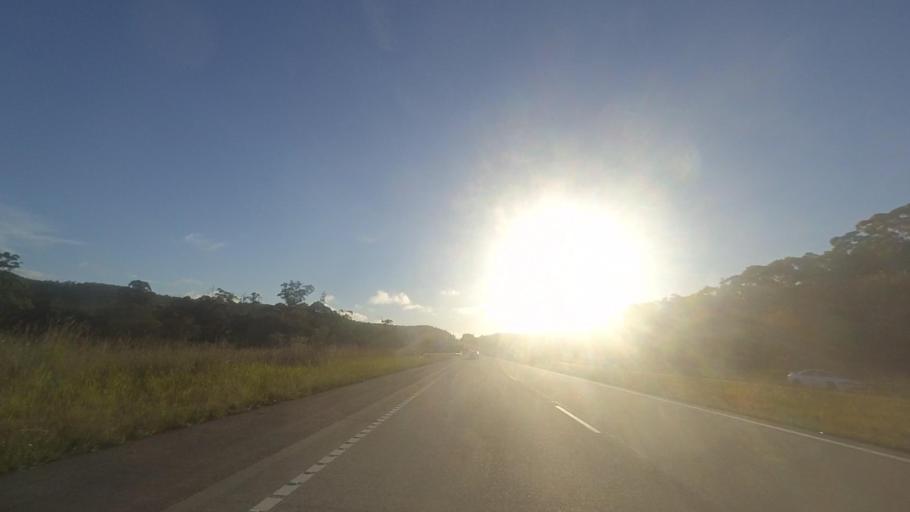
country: AU
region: New South Wales
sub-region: Great Lakes
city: Bulahdelah
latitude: -32.5274
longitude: 152.1915
